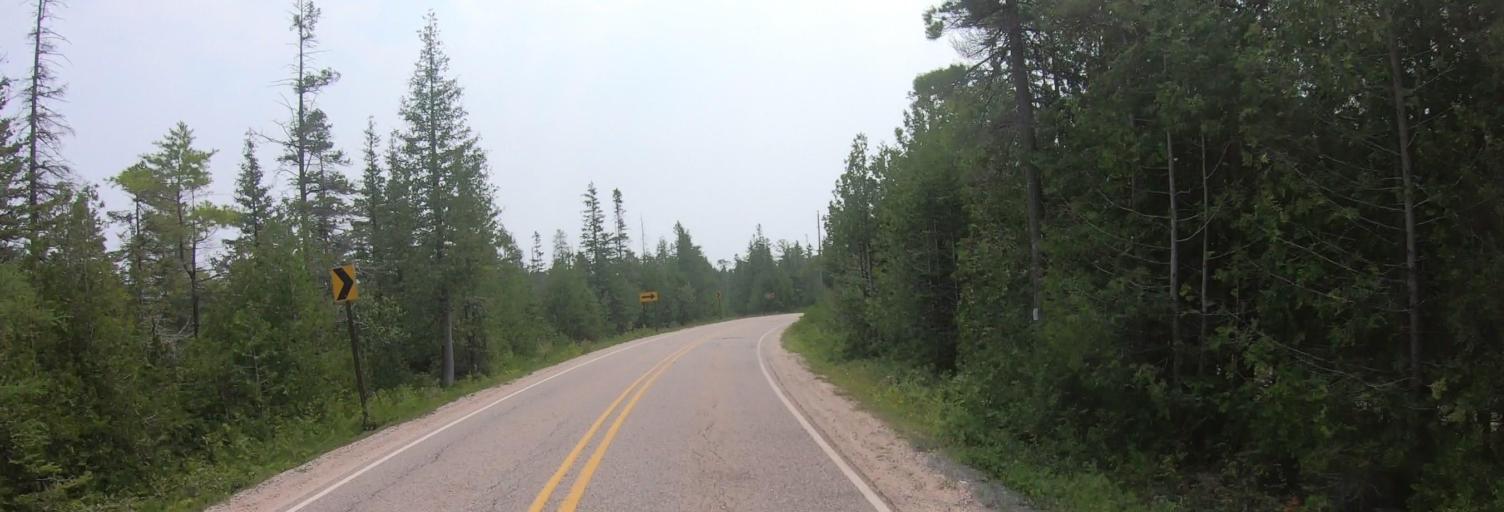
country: CA
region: Ontario
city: Thessalon
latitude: 45.9648
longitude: -83.6341
